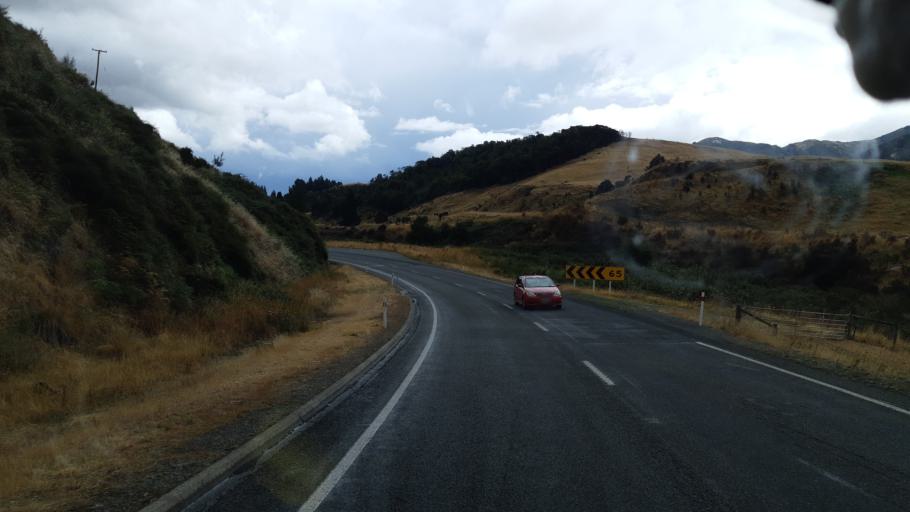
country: NZ
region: Canterbury
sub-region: Hurunui District
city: Amberley
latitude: -42.5952
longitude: 172.5370
